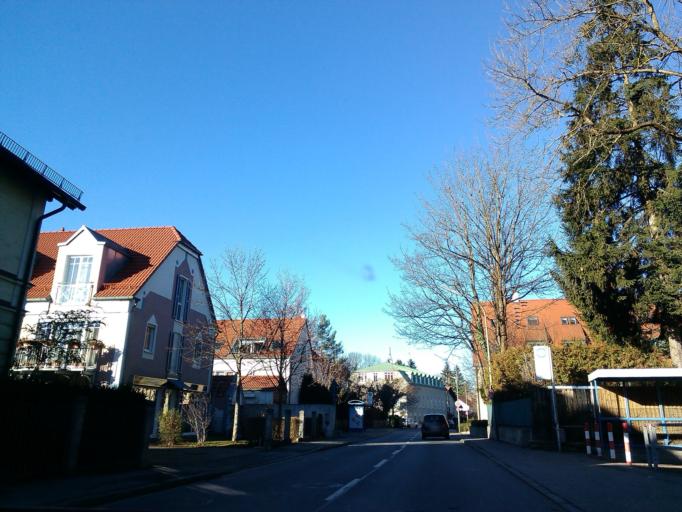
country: DE
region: Bavaria
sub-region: Upper Bavaria
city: Karlsfeld
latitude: 48.1793
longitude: 11.4615
